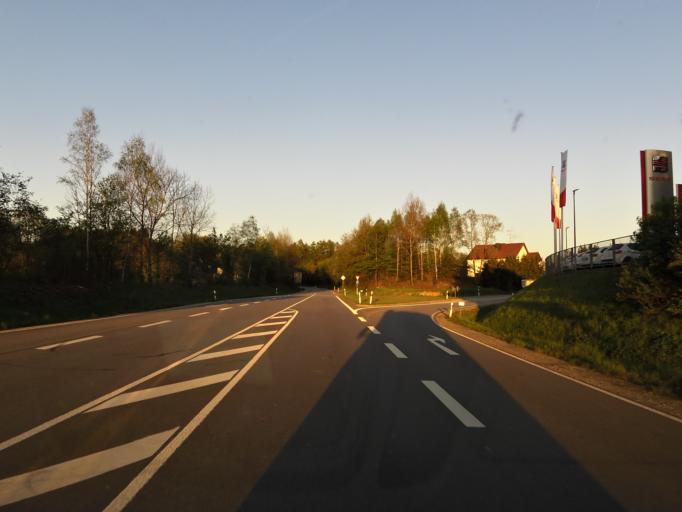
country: DE
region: Bavaria
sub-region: Lower Bavaria
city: Aicha vorm Wald
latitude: 48.6801
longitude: 13.2960
